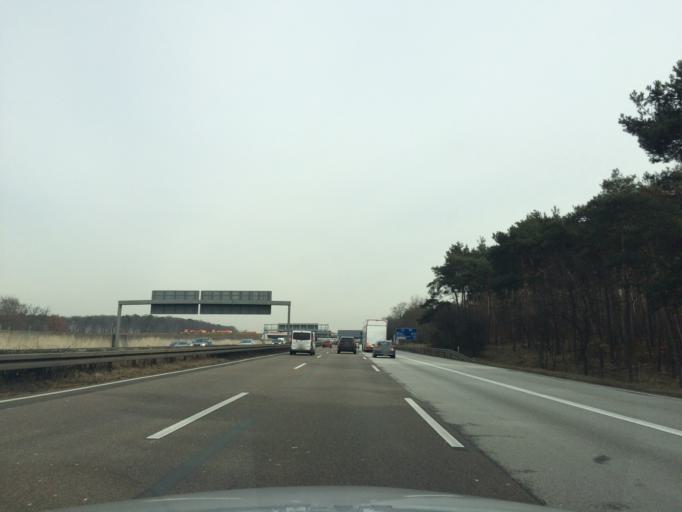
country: DE
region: Hesse
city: Kelsterbach
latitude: 50.0329
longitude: 8.5096
